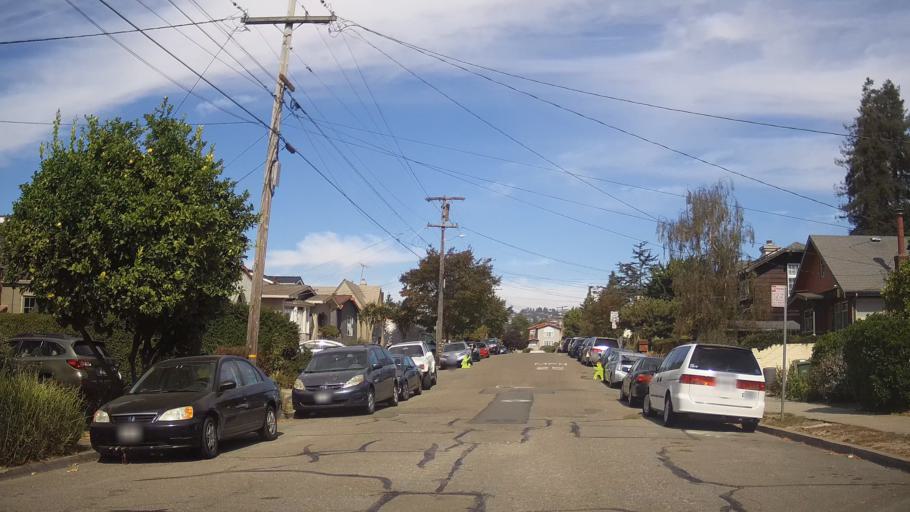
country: US
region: California
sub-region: Alameda County
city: Albany
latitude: 37.8821
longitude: -122.2861
